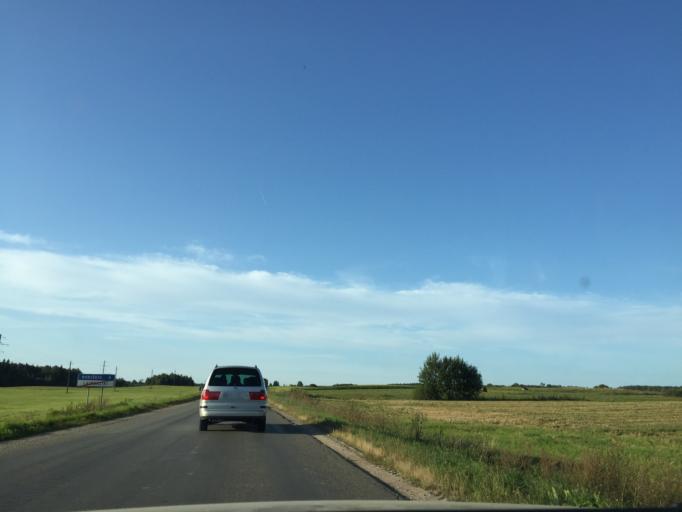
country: LT
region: Panevezys
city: Rokiskis
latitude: 55.9151
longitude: 25.6277
